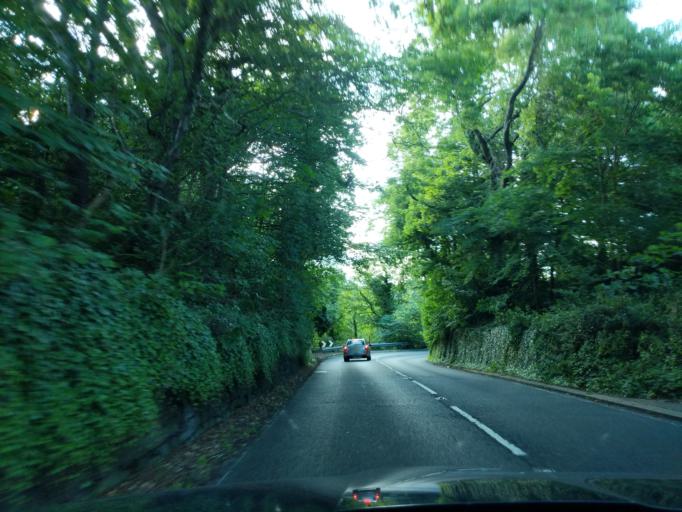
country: GB
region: England
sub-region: Northumberland
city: Bedlington
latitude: 55.1241
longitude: -1.5814
